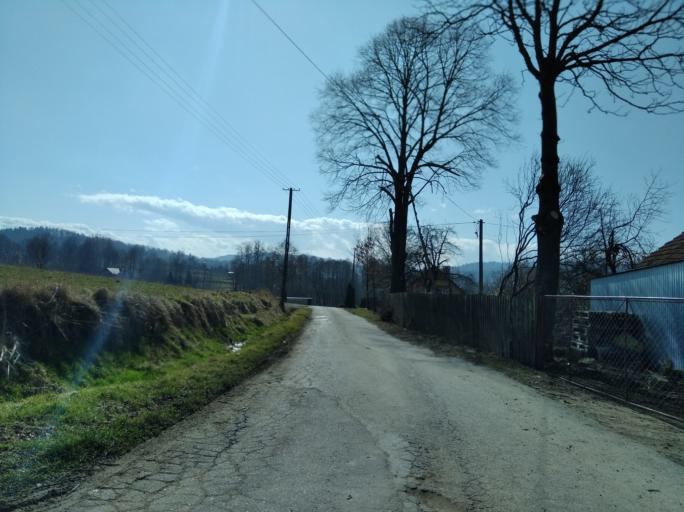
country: PL
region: Subcarpathian Voivodeship
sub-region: Powiat strzyzowski
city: Wysoka Strzyzowska
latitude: 49.8298
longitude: 21.7445
